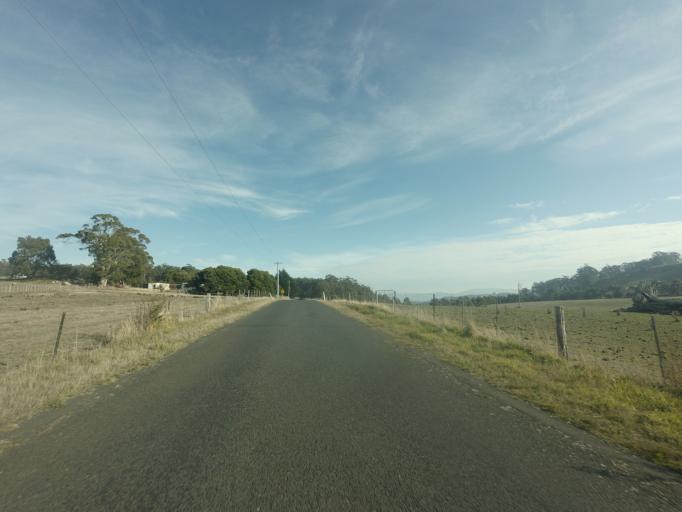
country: AU
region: Tasmania
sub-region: Sorell
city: Sorell
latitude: -42.4806
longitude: 147.4565
